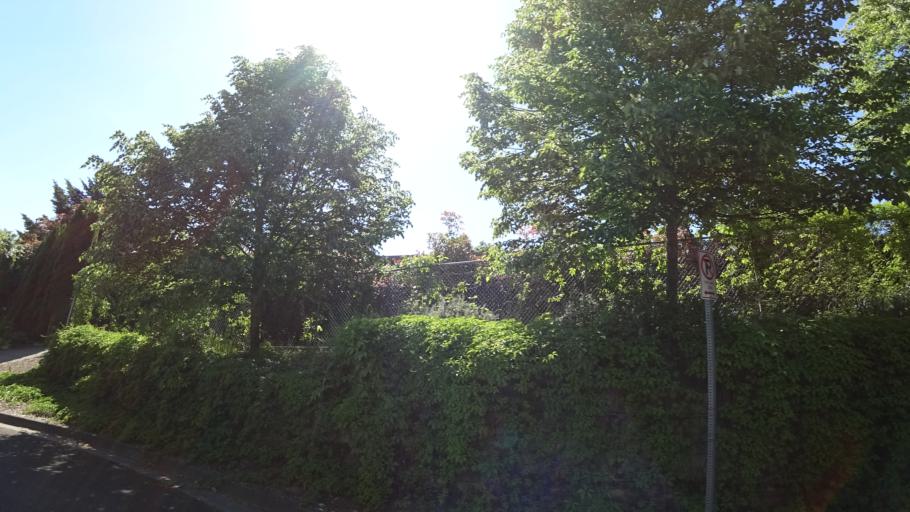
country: US
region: Oregon
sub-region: Washington County
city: Beaverton
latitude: 45.4950
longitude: -122.7984
